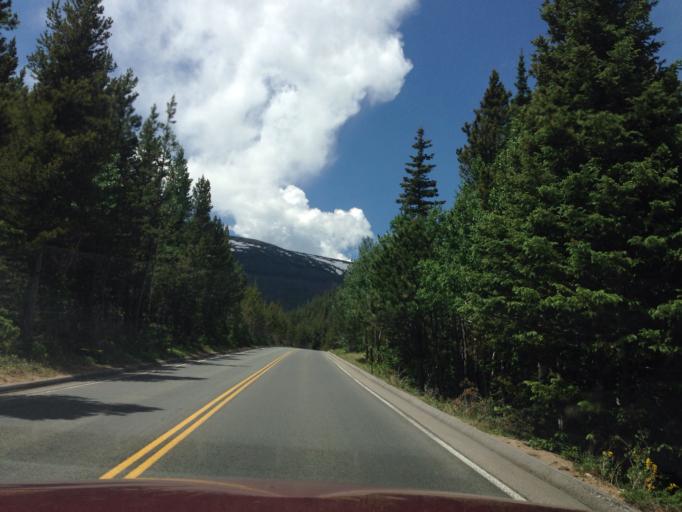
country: US
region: Colorado
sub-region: Larimer County
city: Estes Park
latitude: 40.3982
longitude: -105.6477
